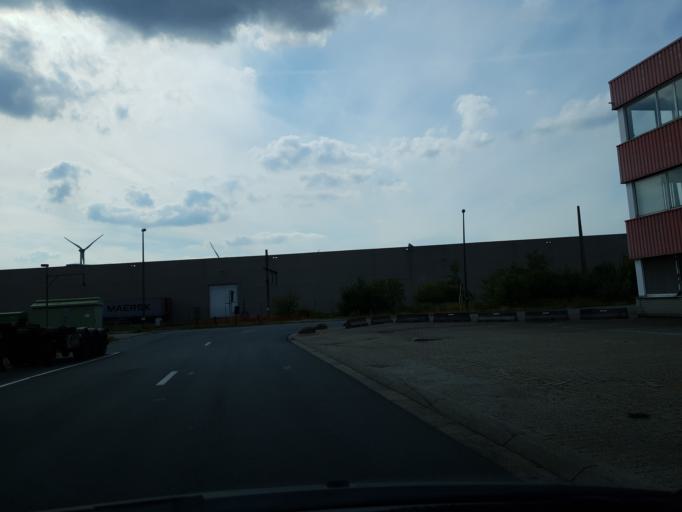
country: BE
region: Flanders
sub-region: Provincie Antwerpen
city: Antwerpen
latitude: 51.2720
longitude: 4.3850
